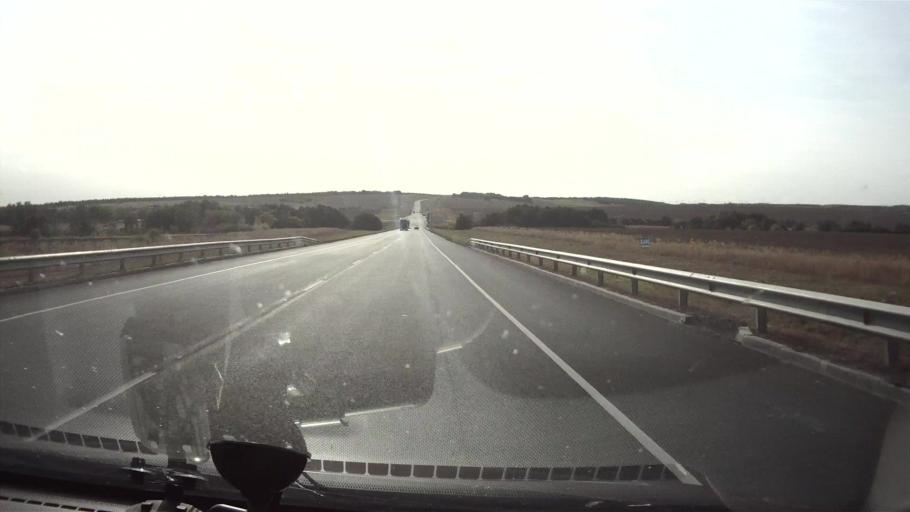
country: RU
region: Saratov
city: Yelshanka
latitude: 51.8274
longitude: 46.3996
